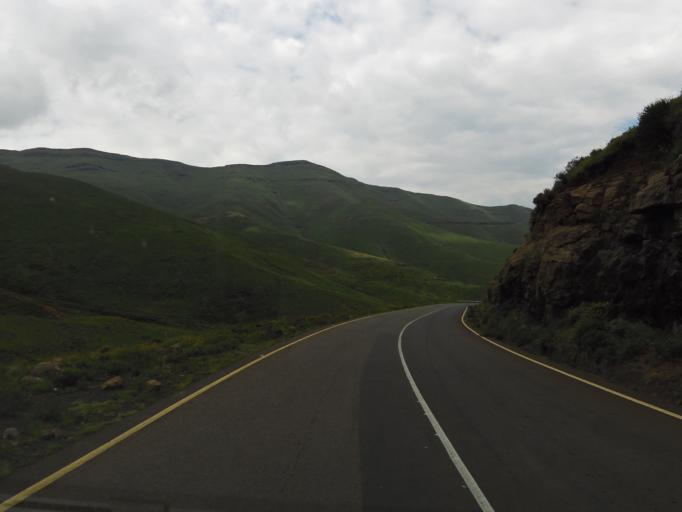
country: LS
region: Butha-Buthe
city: Butha-Buthe
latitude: -29.1128
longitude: 28.4464
